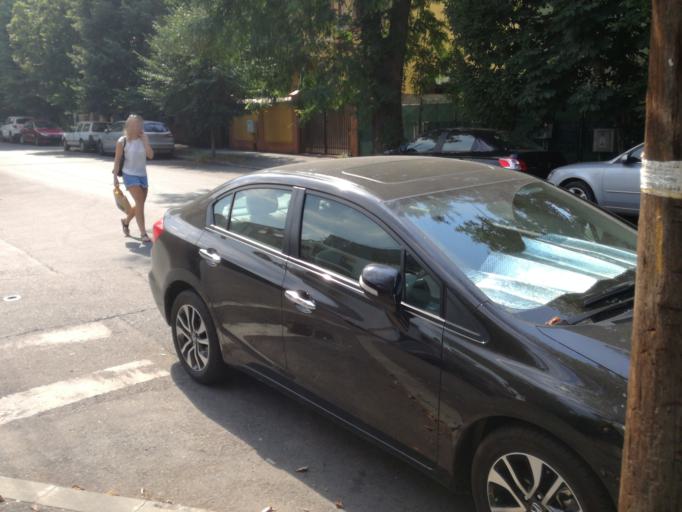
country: RO
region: Bucuresti
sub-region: Municipiul Bucuresti
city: Bucharest
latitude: 44.4589
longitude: 26.1163
